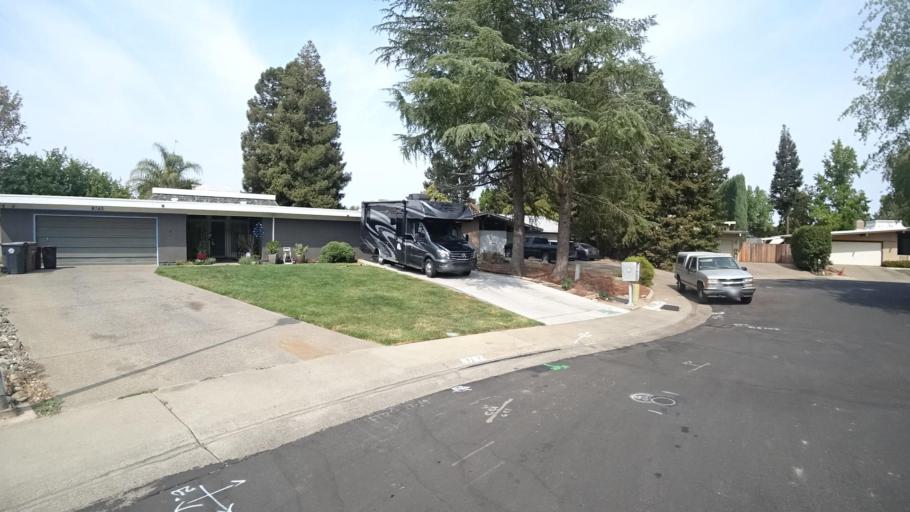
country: US
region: California
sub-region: Sacramento County
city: Elk Grove
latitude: 38.4138
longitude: -121.3772
